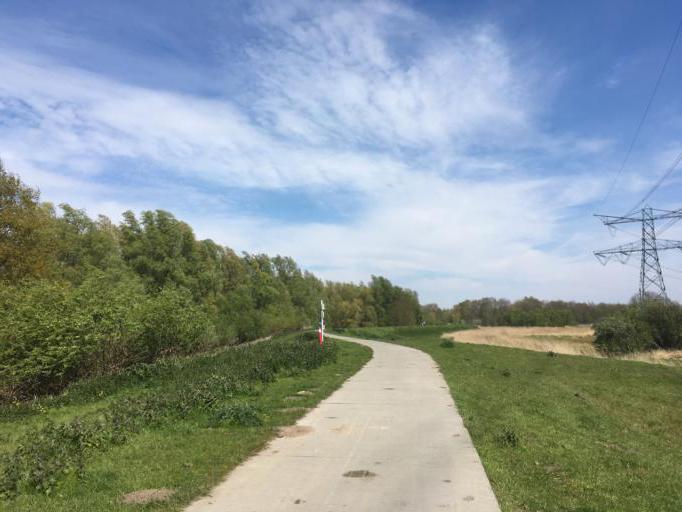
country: NL
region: North Holland
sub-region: Gemeente Weesp
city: Weesp
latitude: 52.3334
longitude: 5.0368
